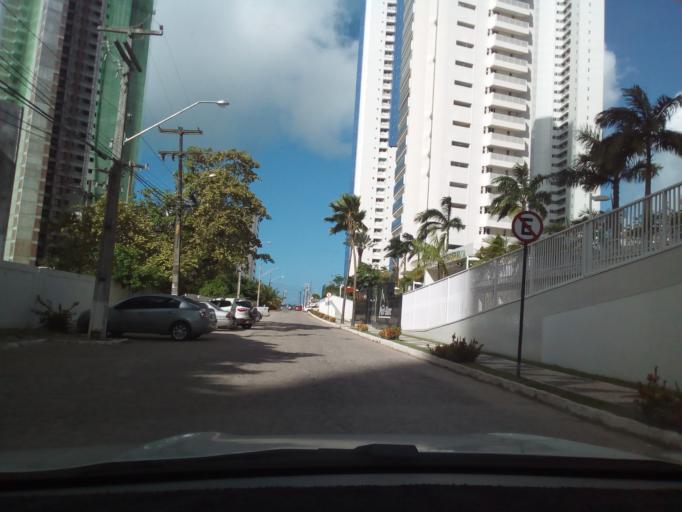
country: BR
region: Paraiba
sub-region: Joao Pessoa
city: Joao Pessoa
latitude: -7.1316
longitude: -34.8289
